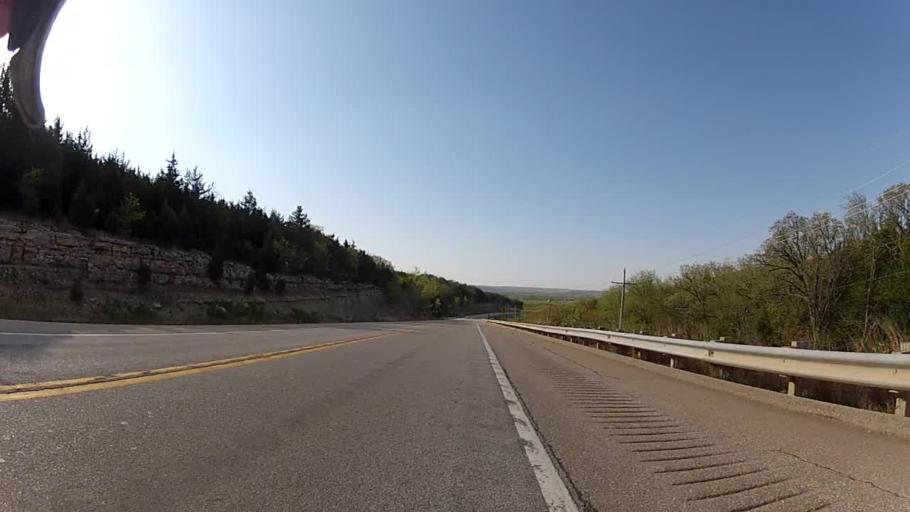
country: US
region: Kansas
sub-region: Riley County
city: Manhattan
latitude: 39.1737
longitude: -96.6459
